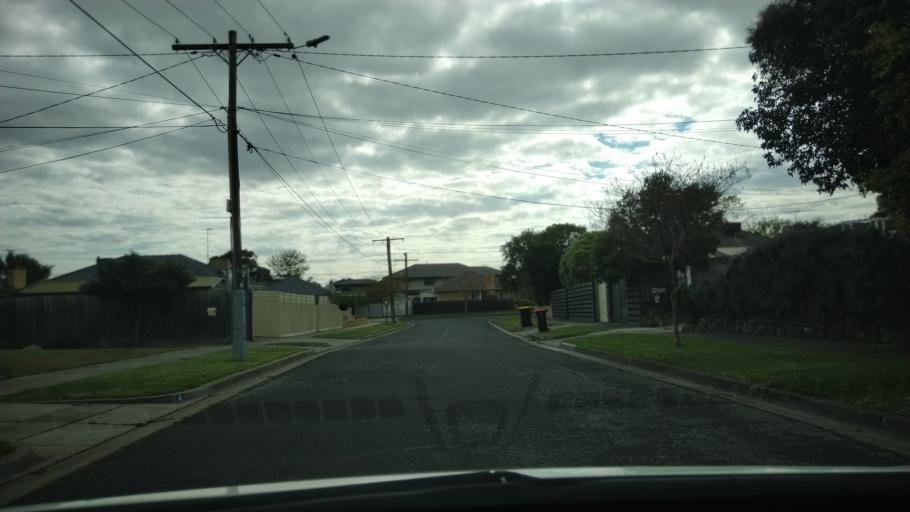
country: AU
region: Victoria
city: Highett
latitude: -37.9560
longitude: 145.0640
